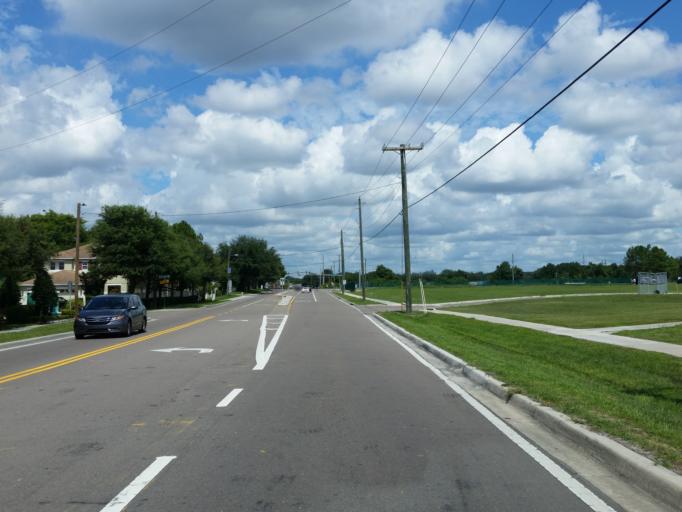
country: US
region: Florida
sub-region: Hillsborough County
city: Riverview
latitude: 27.8507
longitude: -82.3145
